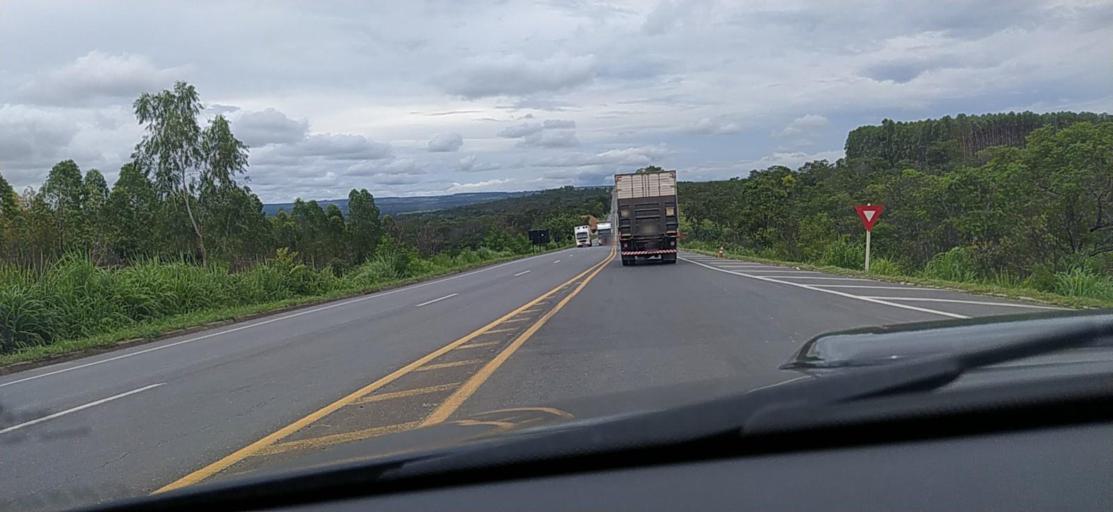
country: BR
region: Minas Gerais
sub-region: Curvelo
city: Curvelo
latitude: -18.7035
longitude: -44.4402
